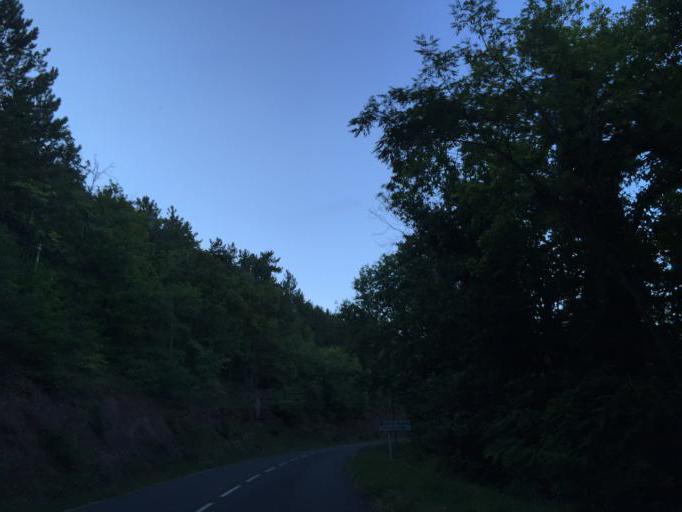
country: FR
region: Midi-Pyrenees
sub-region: Departement de l'Aveyron
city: Saint-Georges-de-Luzencon
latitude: 44.0963
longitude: 2.9005
